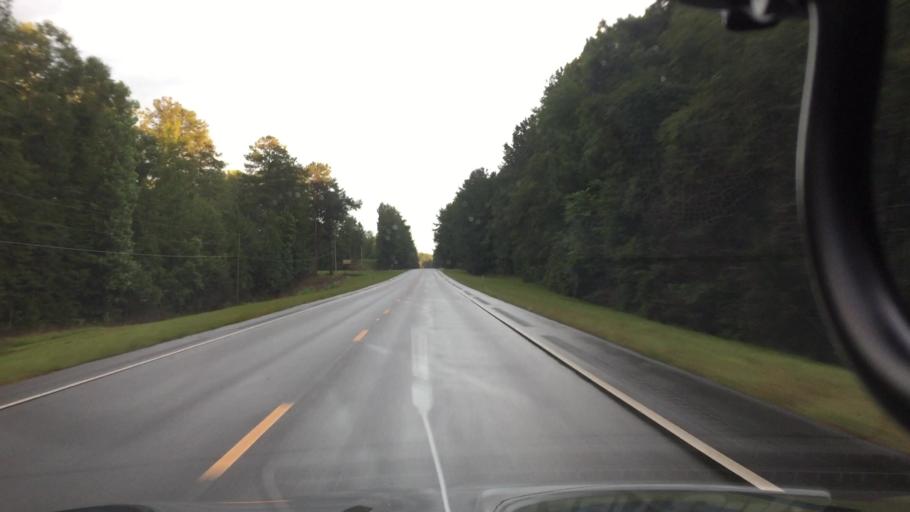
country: US
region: Alabama
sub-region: Coffee County
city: New Brockton
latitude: 31.5632
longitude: -85.9248
